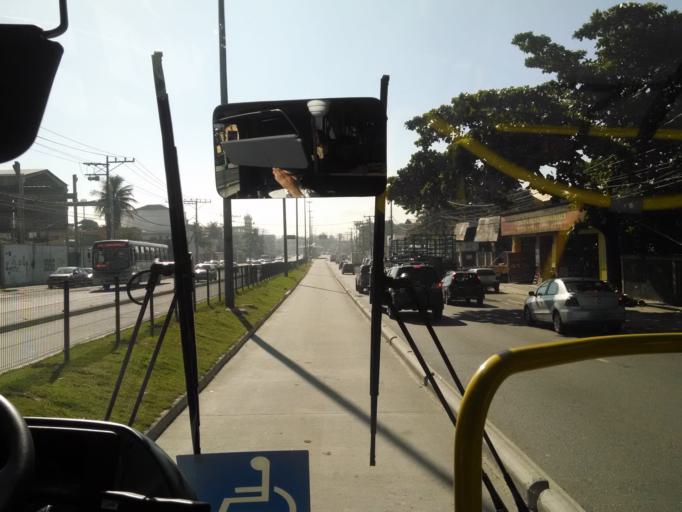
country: BR
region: Rio de Janeiro
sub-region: Sao Joao De Meriti
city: Sao Joao de Meriti
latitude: -22.9571
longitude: -43.3795
